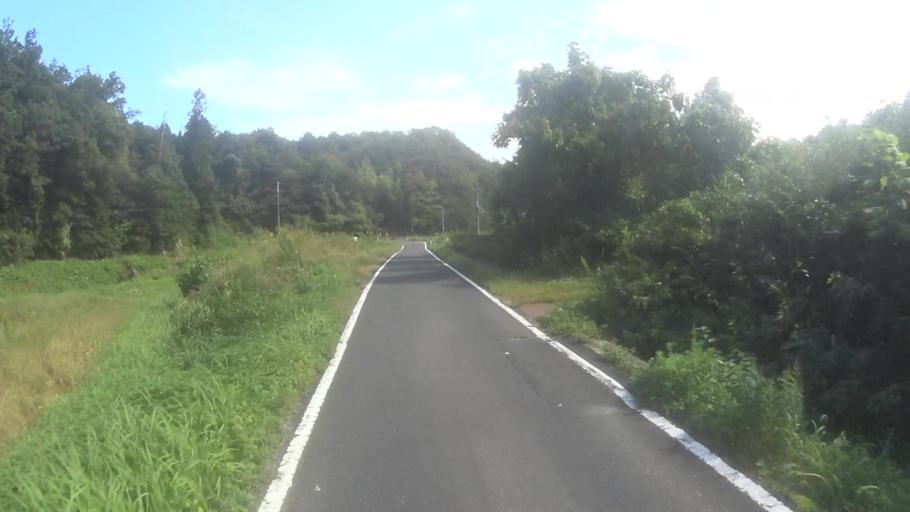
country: JP
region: Kyoto
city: Miyazu
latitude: 35.6040
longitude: 135.0987
